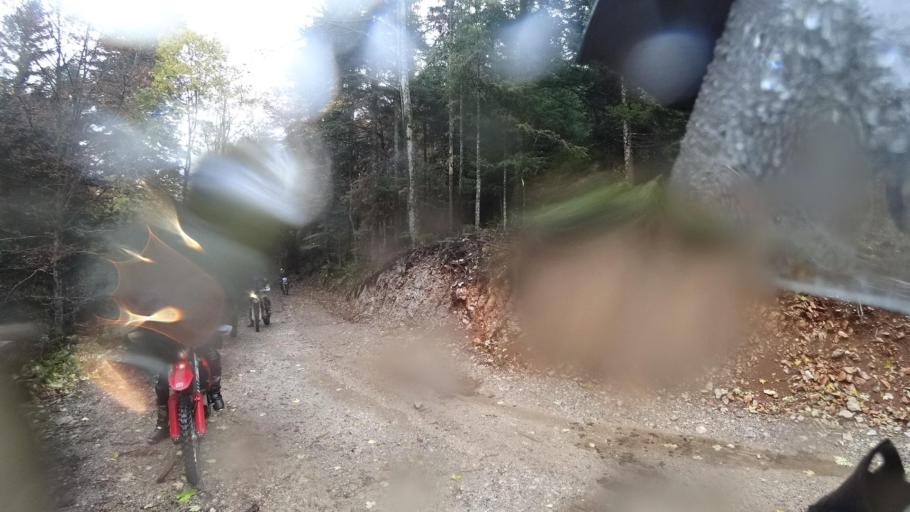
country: HR
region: Primorsko-Goranska
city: Vrbovsko
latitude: 45.3072
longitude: 15.0053
